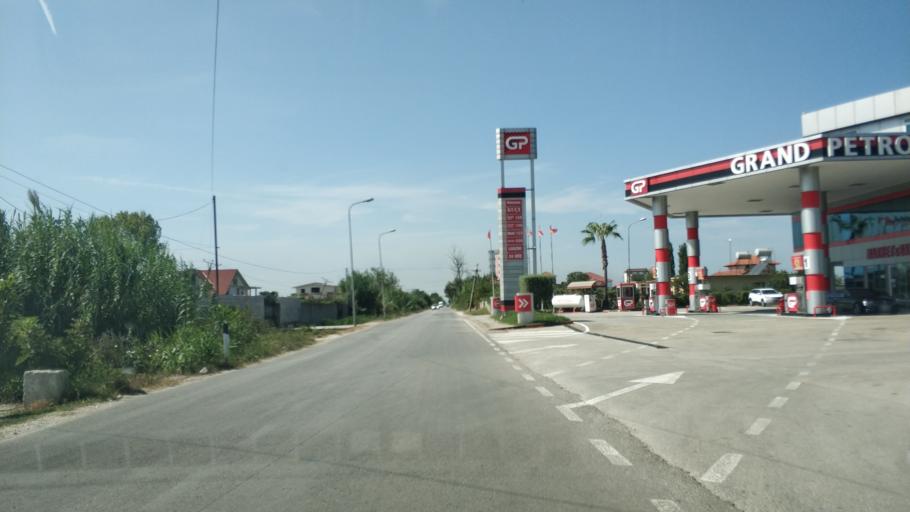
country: AL
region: Fier
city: Fier
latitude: 40.7332
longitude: 19.5321
